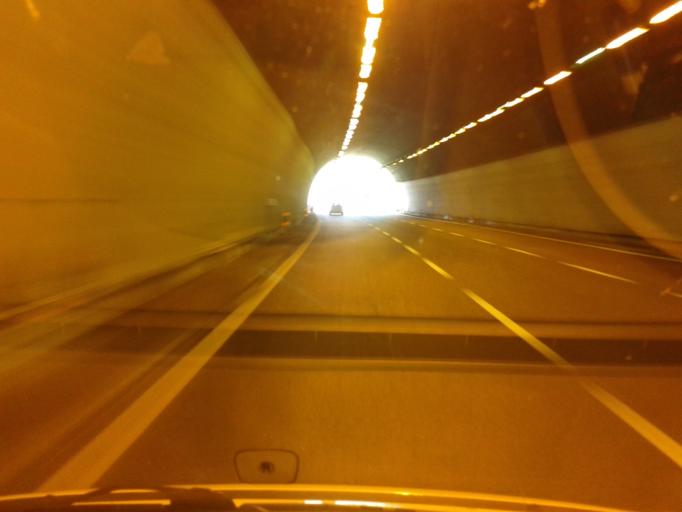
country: IT
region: Liguria
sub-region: Provincia di Genova
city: Mele
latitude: 44.4691
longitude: 8.7418
